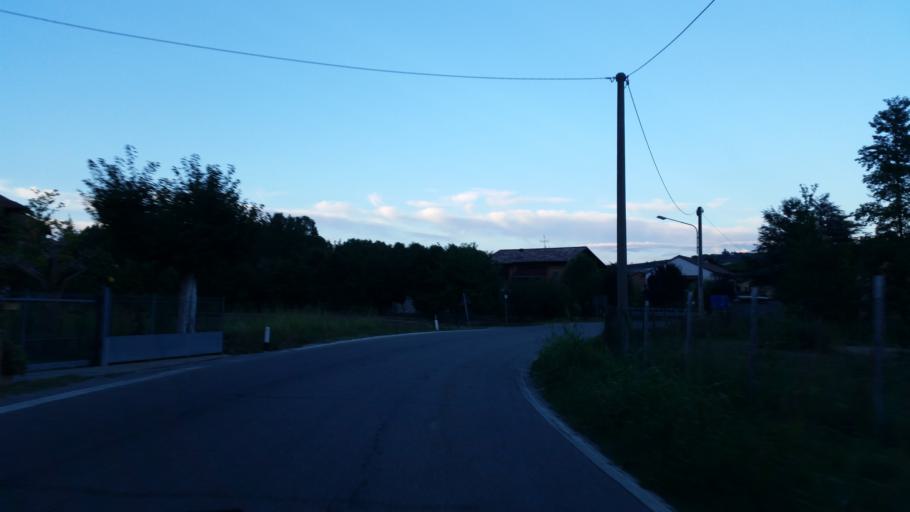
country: IT
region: Piedmont
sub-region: Provincia di Cuneo
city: Neive-Borgonovo
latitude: 44.7099
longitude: 8.1062
